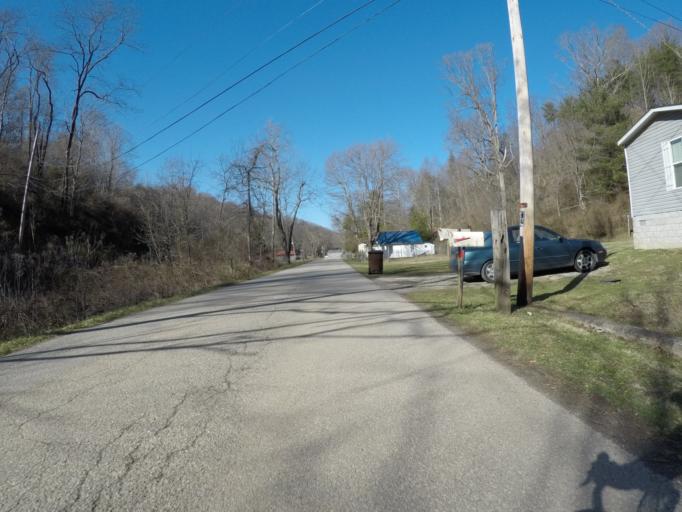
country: US
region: Kentucky
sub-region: Boyd County
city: Catlettsburg
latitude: 38.4091
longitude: -82.6384
